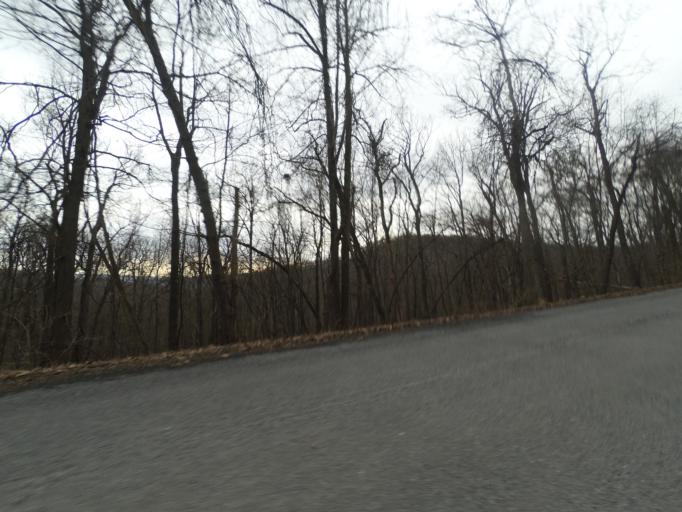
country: US
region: Pennsylvania
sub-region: Centre County
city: Stormstown
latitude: 40.8703
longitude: -78.0056
